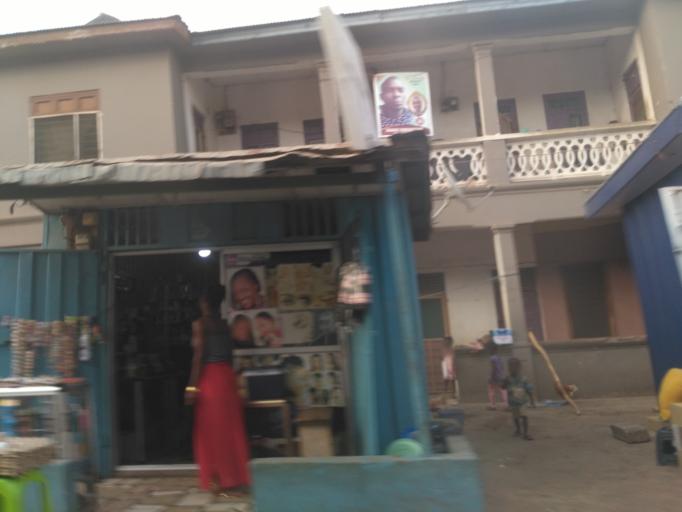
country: GH
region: Ashanti
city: Kumasi
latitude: 6.7088
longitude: -1.6197
